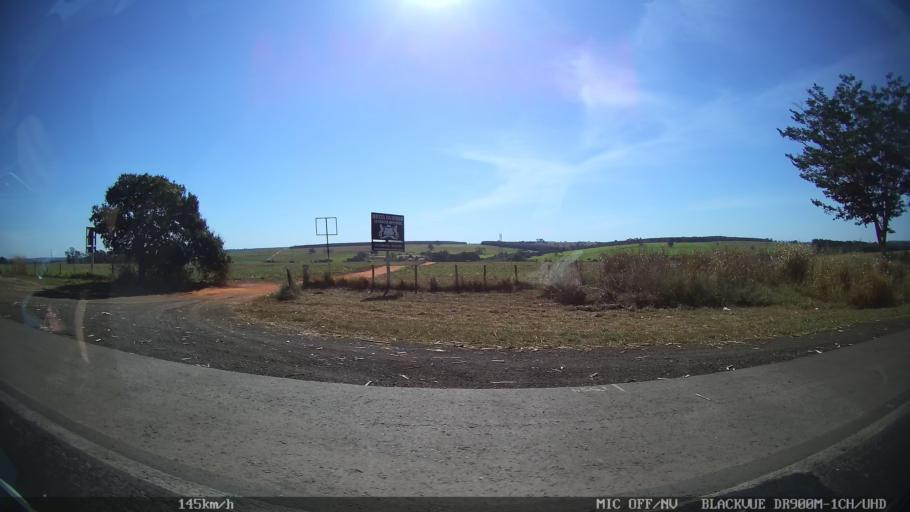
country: BR
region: Sao Paulo
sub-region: Olimpia
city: Olimpia
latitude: -20.6781
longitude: -48.8905
